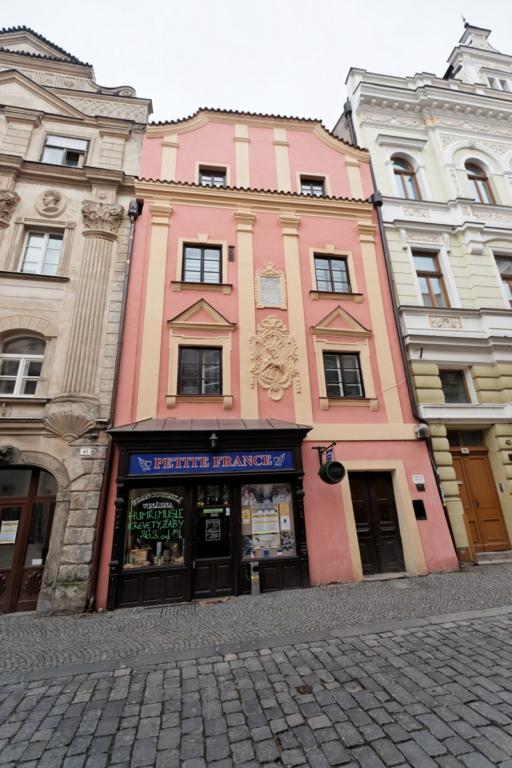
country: CZ
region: Pardubicky
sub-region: Okres Pardubice
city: Pardubice
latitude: 50.0392
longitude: 15.7796
